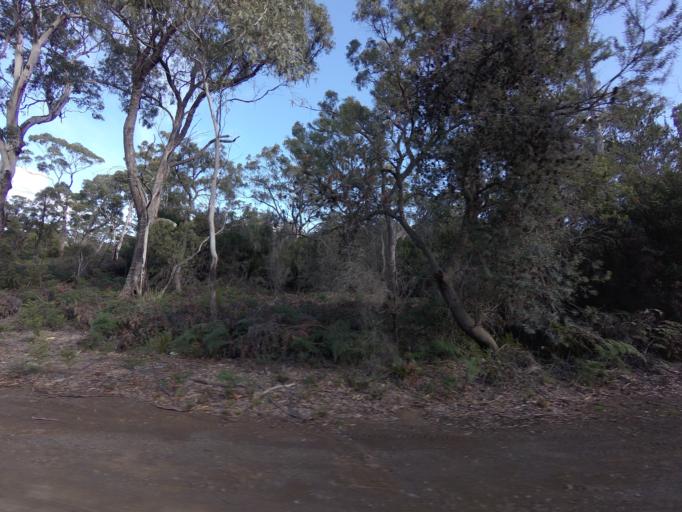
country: AU
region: Tasmania
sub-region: Clarence
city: Sandford
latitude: -42.9900
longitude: 147.7145
